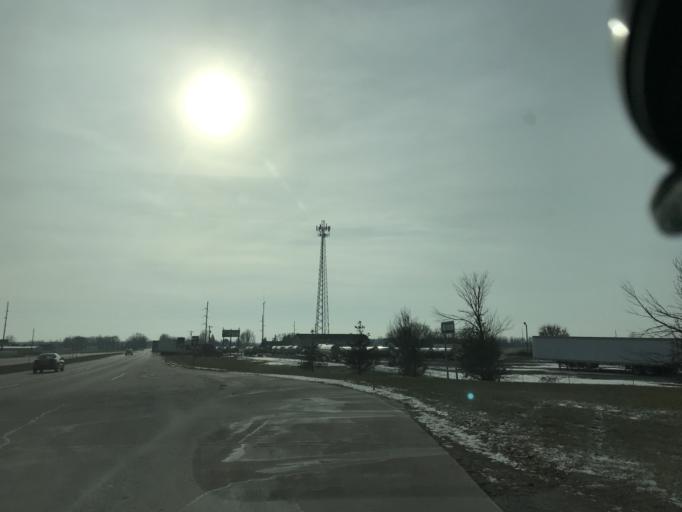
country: US
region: Michigan
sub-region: Ionia County
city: Ionia
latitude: 42.8768
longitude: -85.0751
